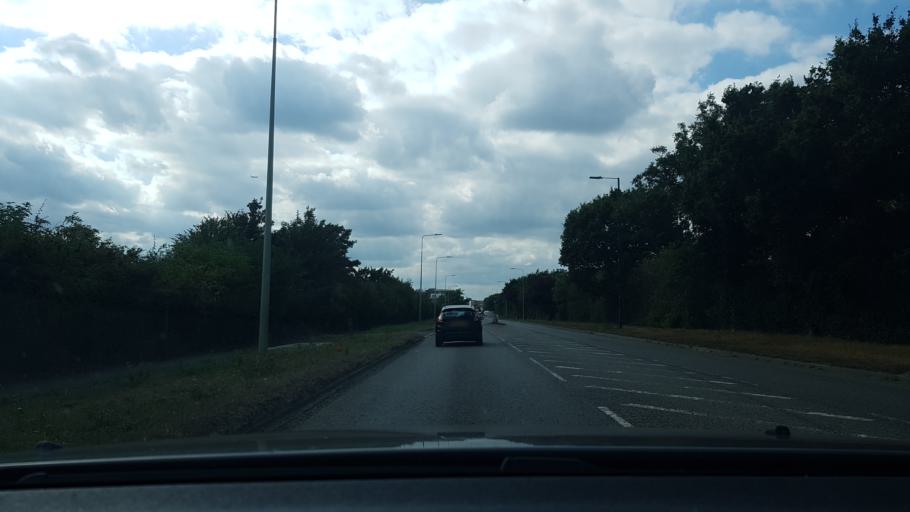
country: GB
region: England
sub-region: Surrey
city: Colnbrook
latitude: 51.4873
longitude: -0.5258
